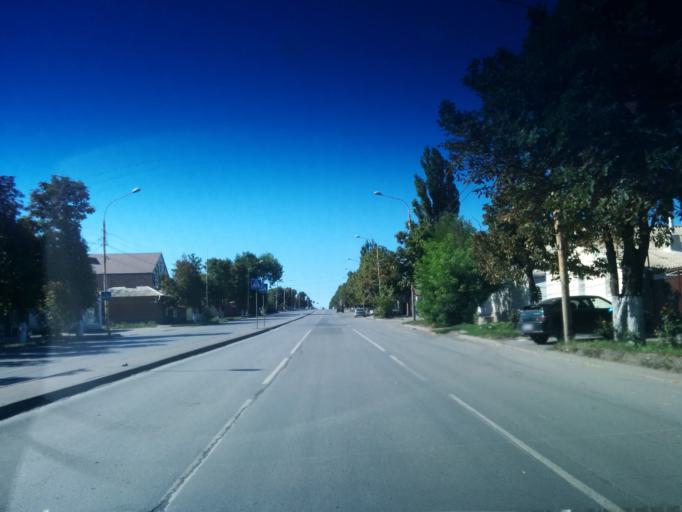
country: RU
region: Rostov
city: Shakhty
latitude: 47.6992
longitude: 40.2356
